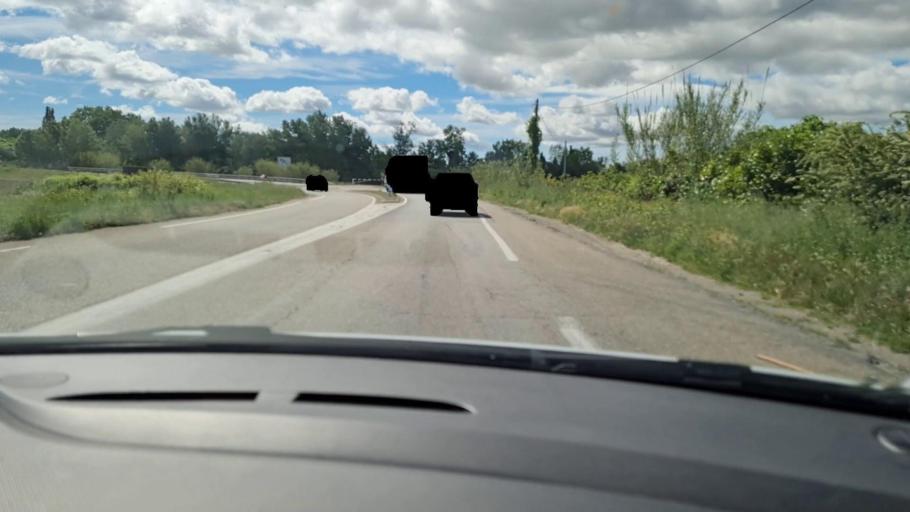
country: FR
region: Languedoc-Roussillon
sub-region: Departement du Gard
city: Caissargues
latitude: 43.7932
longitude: 4.3469
